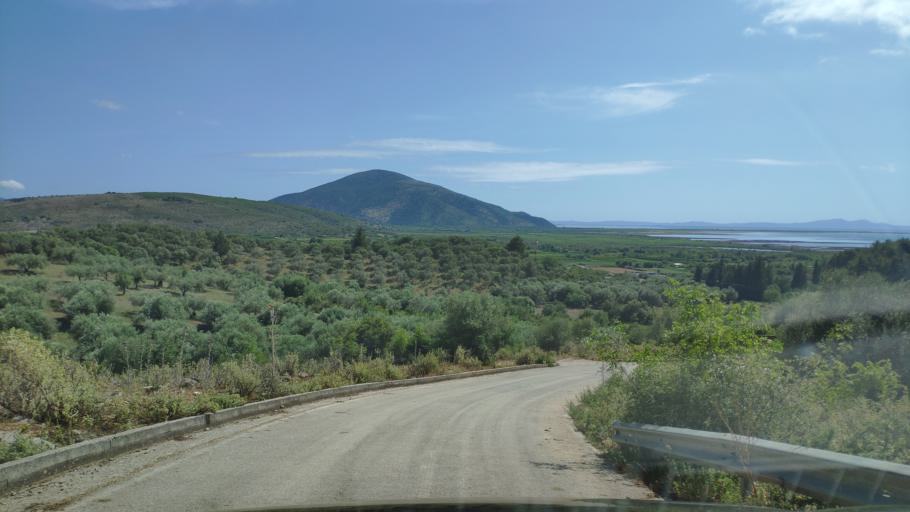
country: AL
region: Vlore
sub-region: Rrethi i Sarandes
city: Konispol
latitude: 39.6238
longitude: 20.2037
